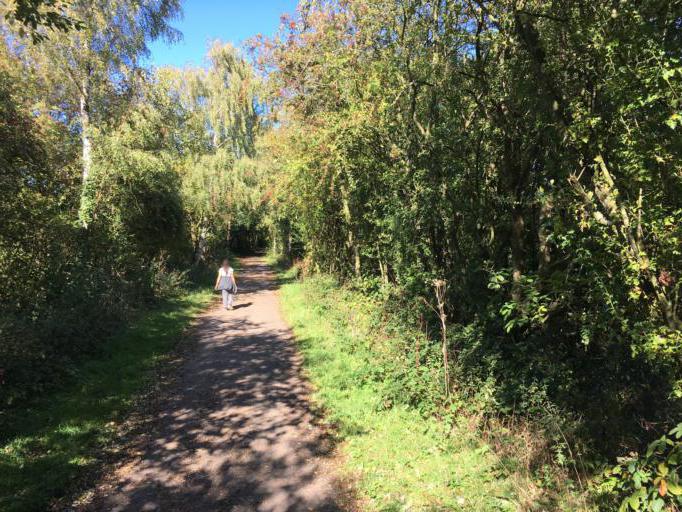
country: GB
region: England
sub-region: Warwickshire
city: Kenilworth
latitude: 52.3743
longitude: -1.5976
